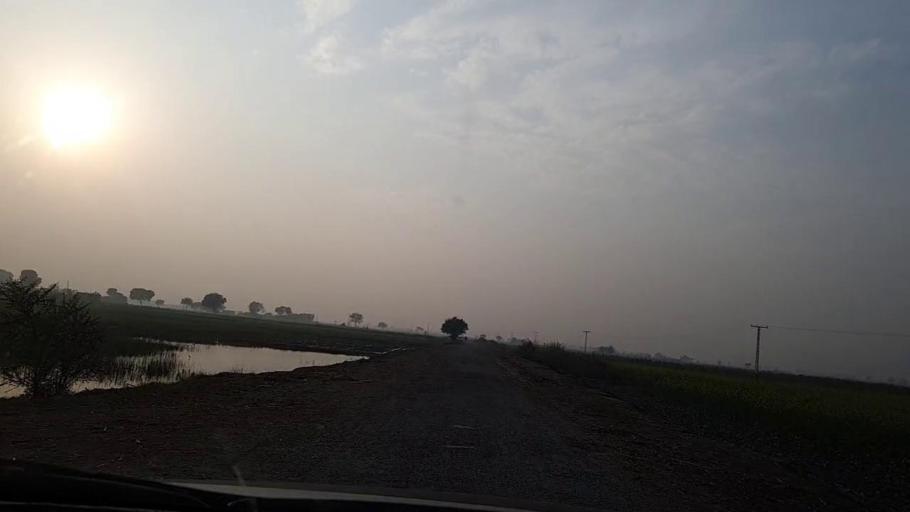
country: PK
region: Sindh
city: Nawabshah
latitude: 26.2979
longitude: 68.2677
